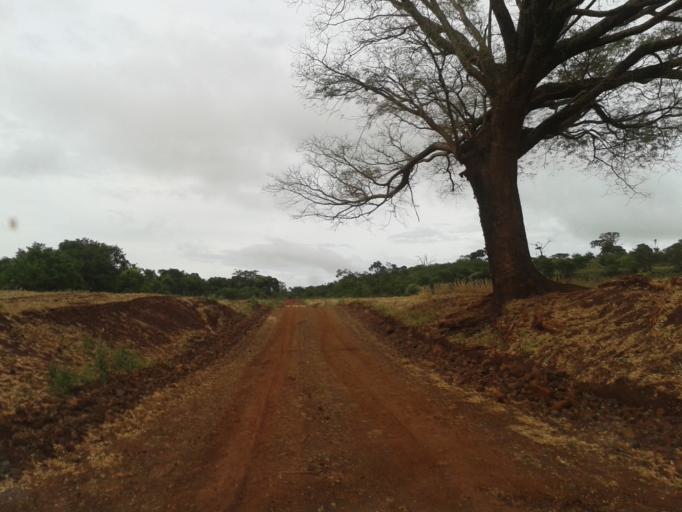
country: BR
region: Minas Gerais
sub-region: Capinopolis
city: Capinopolis
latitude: -18.7333
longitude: -49.7752
